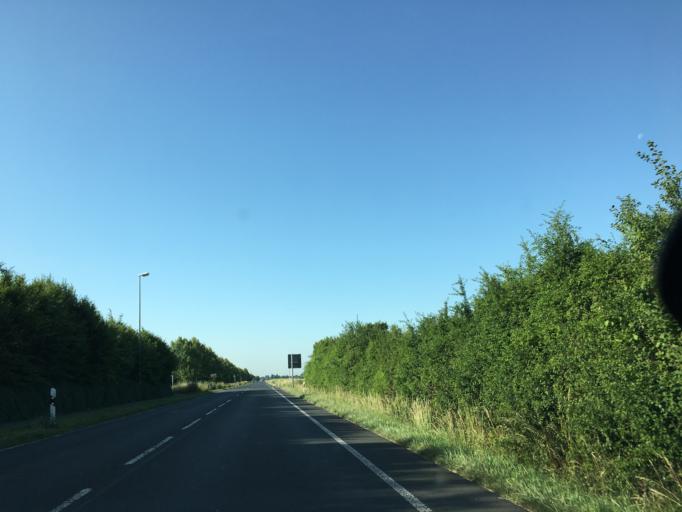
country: DE
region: Hesse
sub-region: Regierungsbezirk Darmstadt
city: Gross-Gerau
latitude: 49.8981
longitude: 8.4802
